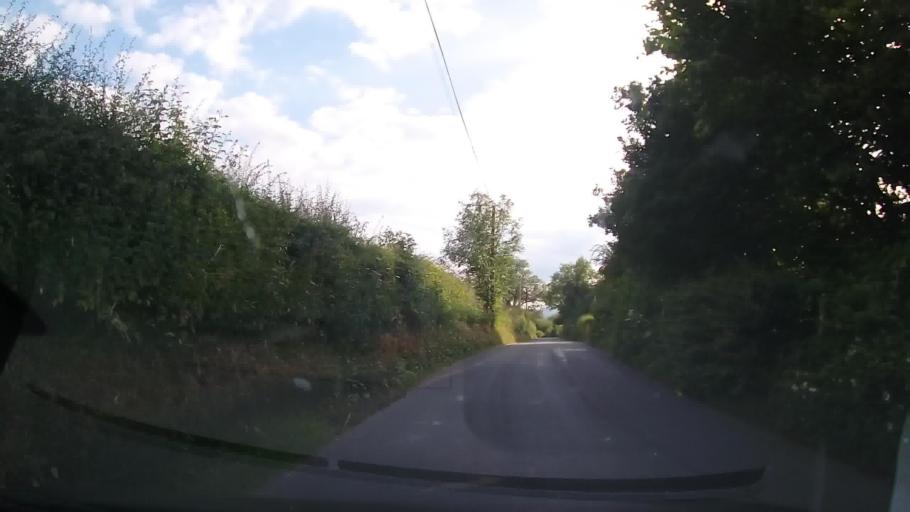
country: GB
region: Wales
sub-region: Gwynedd
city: Bala
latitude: 52.9004
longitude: -3.5965
